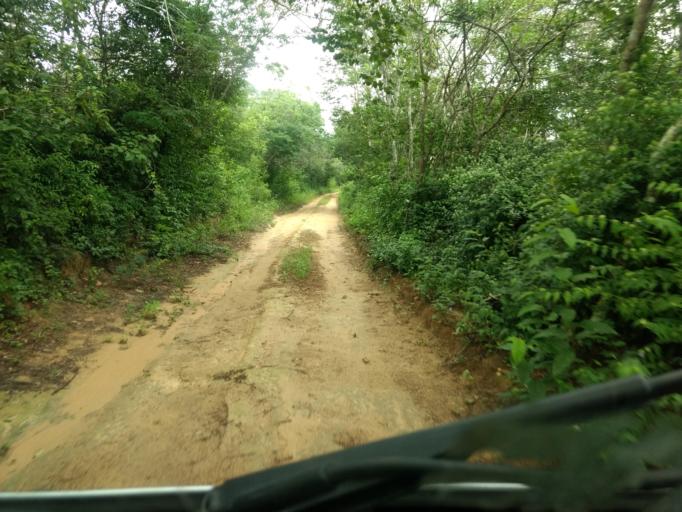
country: BR
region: Ceara
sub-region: Crateus
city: Crateus
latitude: -5.1773
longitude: -40.9370
